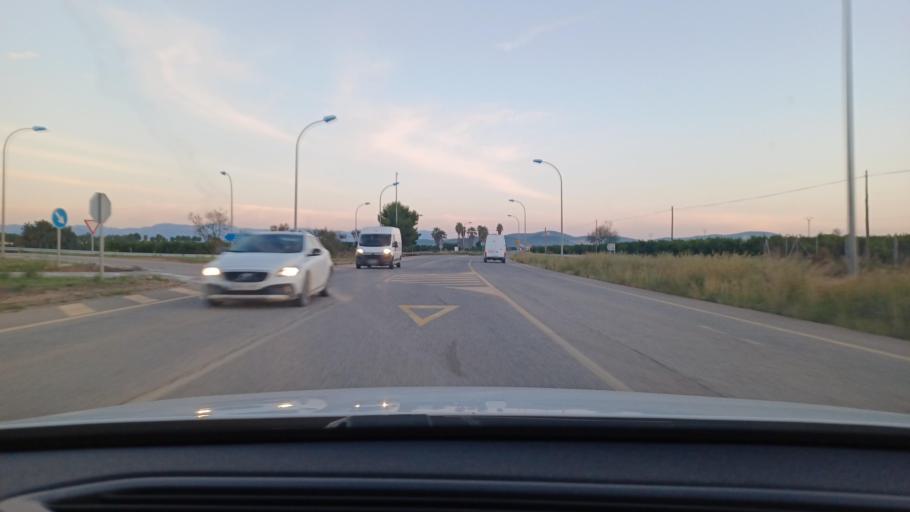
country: ES
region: Catalonia
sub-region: Provincia de Tarragona
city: Ulldecona
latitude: 40.5535
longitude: 0.4321
